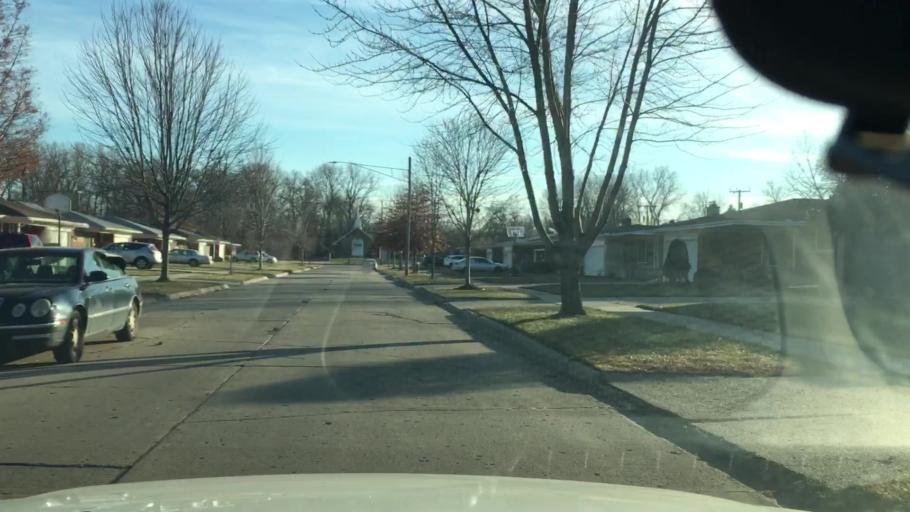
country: US
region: Michigan
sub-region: Oakland County
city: Madison Heights
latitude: 42.4998
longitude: -83.0773
